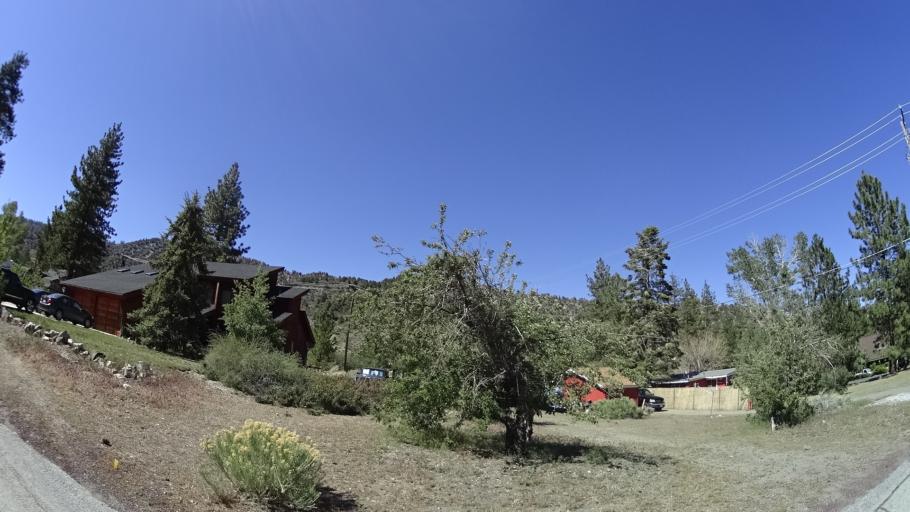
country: US
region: California
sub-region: San Bernardino County
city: Wrightwood
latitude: 34.3652
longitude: -117.6526
